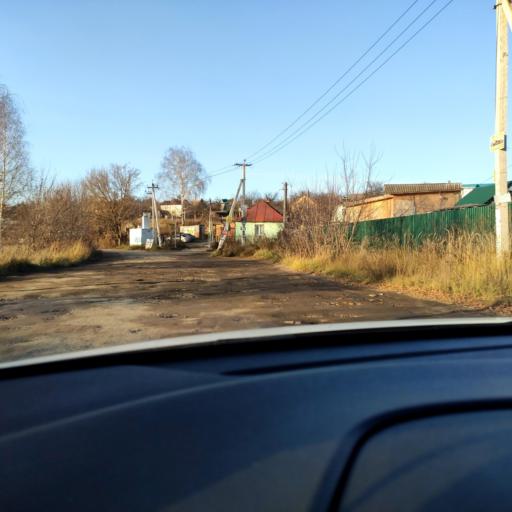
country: RU
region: Tatarstan
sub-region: Gorod Kazan'
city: Kazan
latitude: 55.8845
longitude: 49.0691
